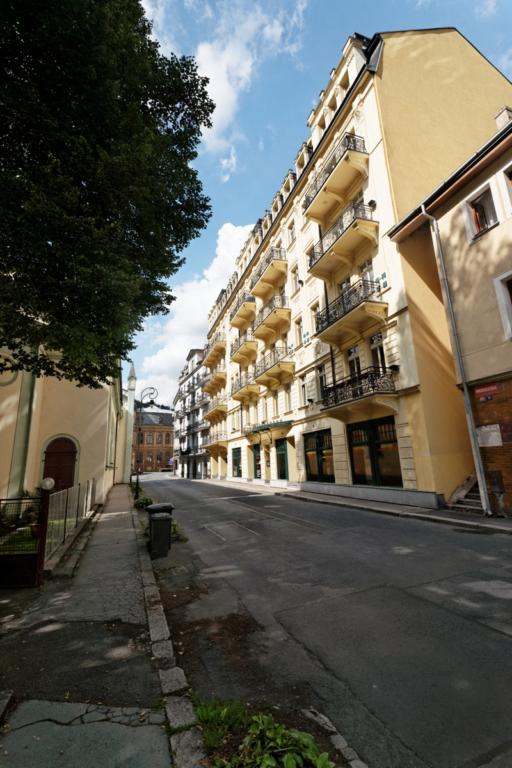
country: CZ
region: Karlovarsky
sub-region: Okres Karlovy Vary
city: Karlovy Vary
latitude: 50.2182
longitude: 12.8835
